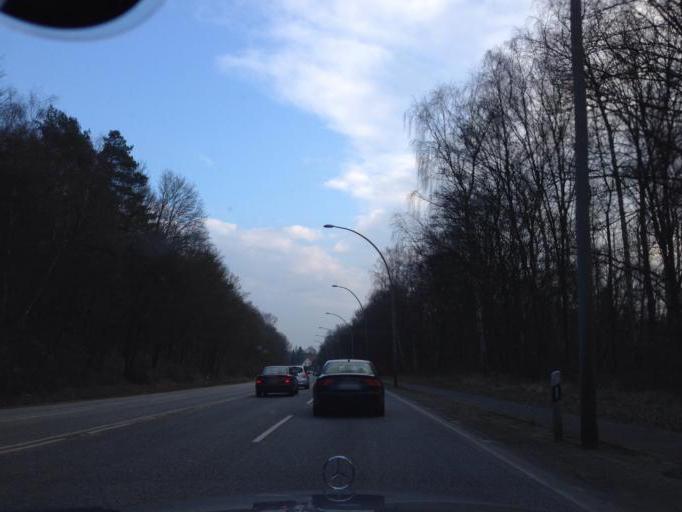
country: DE
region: Hamburg
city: Bergedorf
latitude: 53.4990
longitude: 10.1879
